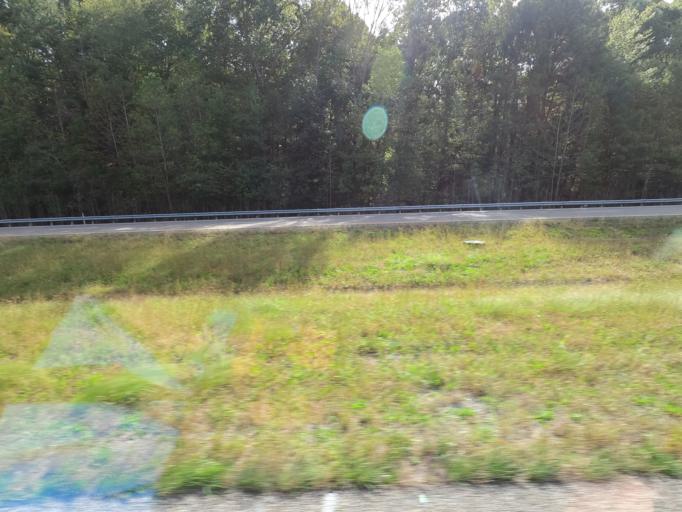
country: US
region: Tennessee
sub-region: Humphreys County
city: New Johnsonville
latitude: 35.8793
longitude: -87.8468
